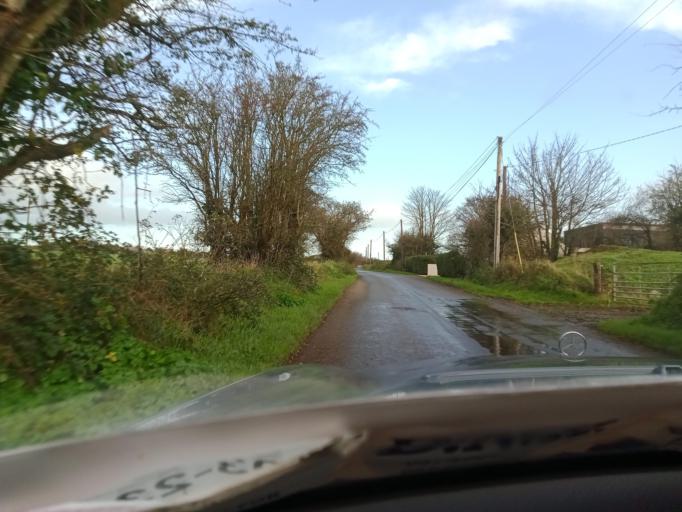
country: IE
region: Leinster
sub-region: Kilkenny
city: Mooncoin
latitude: 52.2843
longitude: -7.2551
